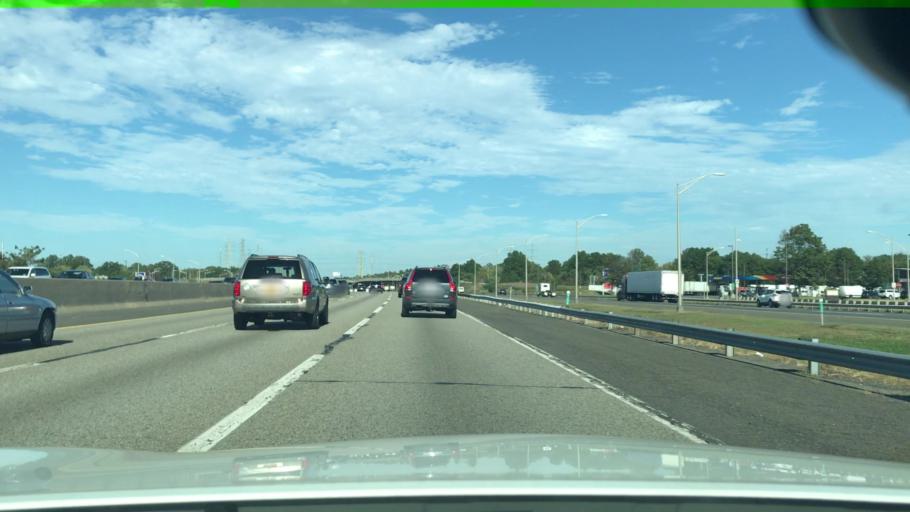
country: US
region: New Jersey
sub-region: Middlesex County
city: Sewaren
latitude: 40.5566
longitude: -74.2659
